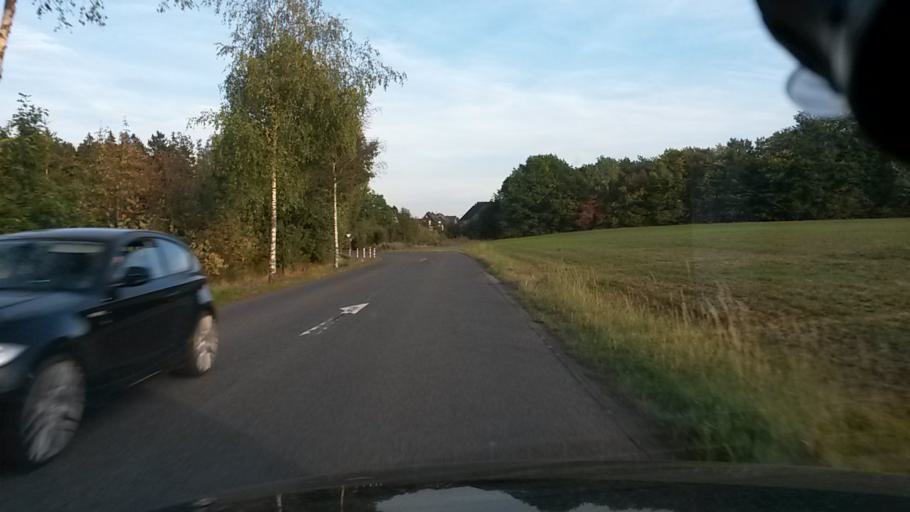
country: DE
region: North Rhine-Westphalia
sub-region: Regierungsbezirk Koln
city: Marienheide
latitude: 51.0714
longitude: 7.5687
